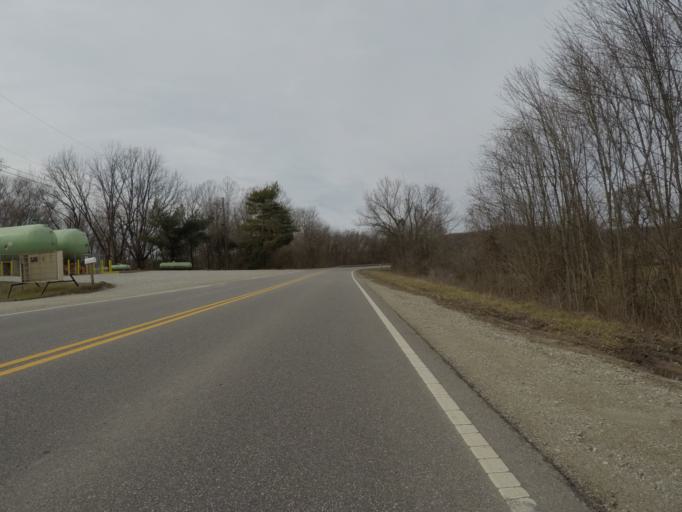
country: US
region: West Virginia
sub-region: Cabell County
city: Pea Ridge
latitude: 38.4414
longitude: -82.3730
